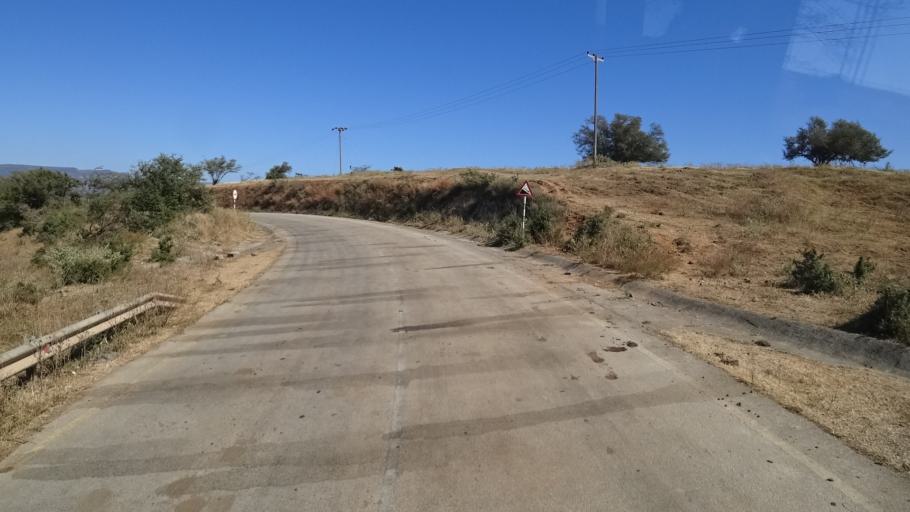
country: YE
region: Al Mahrah
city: Hawf
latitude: 16.7449
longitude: 53.3945
